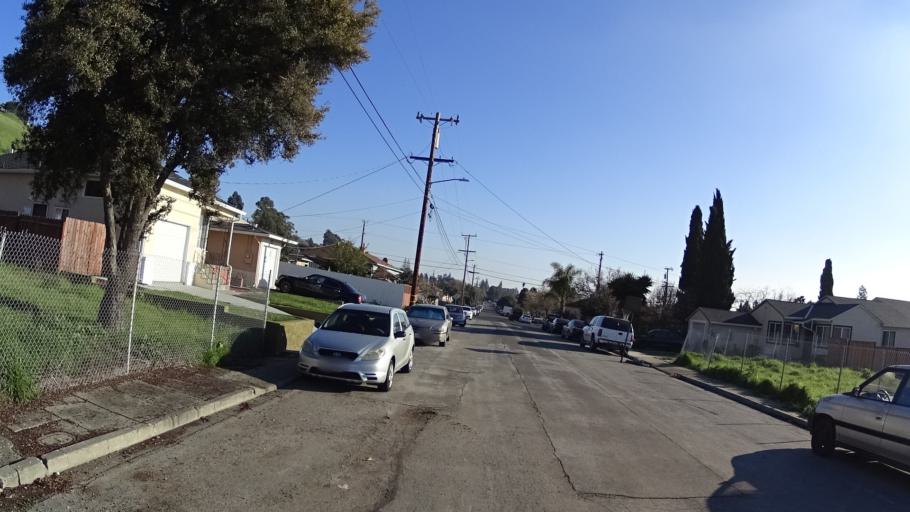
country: US
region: California
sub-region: Alameda County
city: Hayward
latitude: 37.6588
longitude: -122.0718
